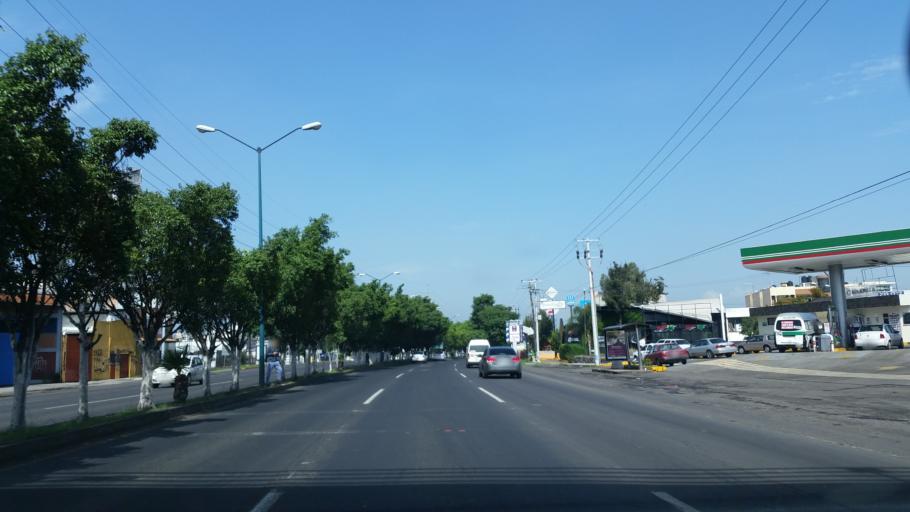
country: MX
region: Michoacan
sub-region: Morelia
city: Morelos
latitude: 19.6770
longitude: -101.2217
